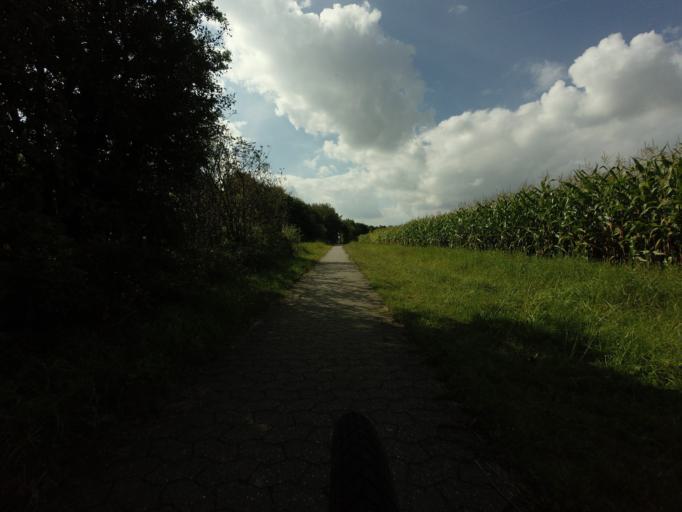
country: DK
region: Central Jutland
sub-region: Viborg Kommune
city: Karup
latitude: 56.3283
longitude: 9.2255
